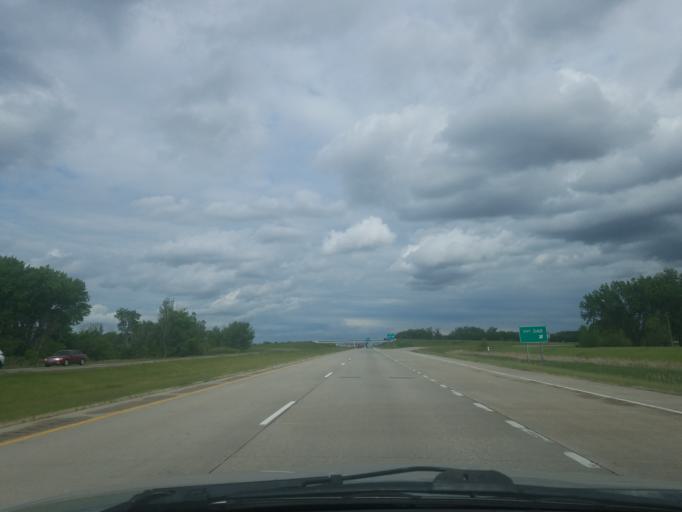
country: US
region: North Dakota
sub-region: Cass County
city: West Fargo
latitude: 46.8775
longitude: -96.9757
